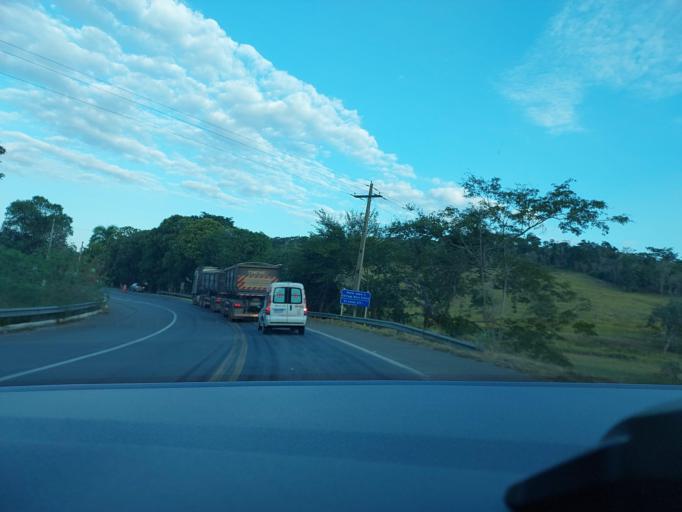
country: BR
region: Minas Gerais
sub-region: Muriae
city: Muriae
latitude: -21.1454
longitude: -42.1690
